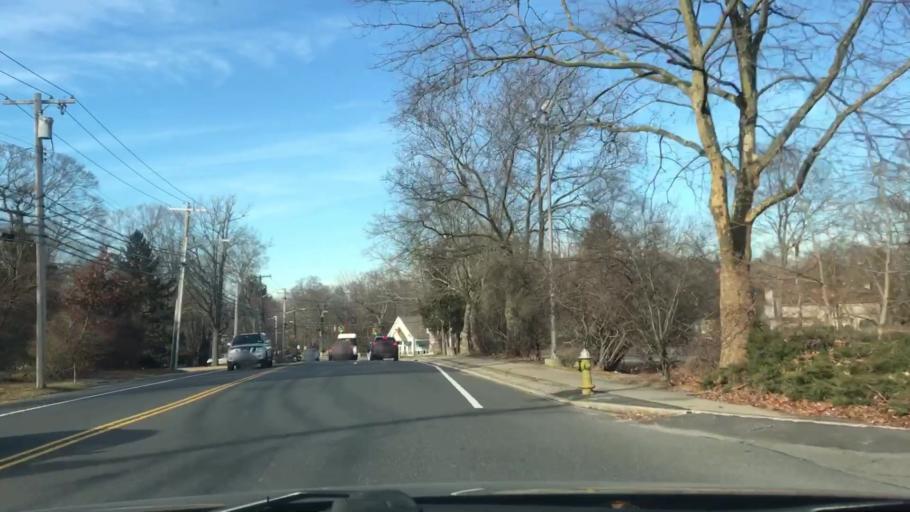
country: US
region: New York
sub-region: Suffolk County
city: Lake Grove
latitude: 40.8360
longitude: -73.1098
